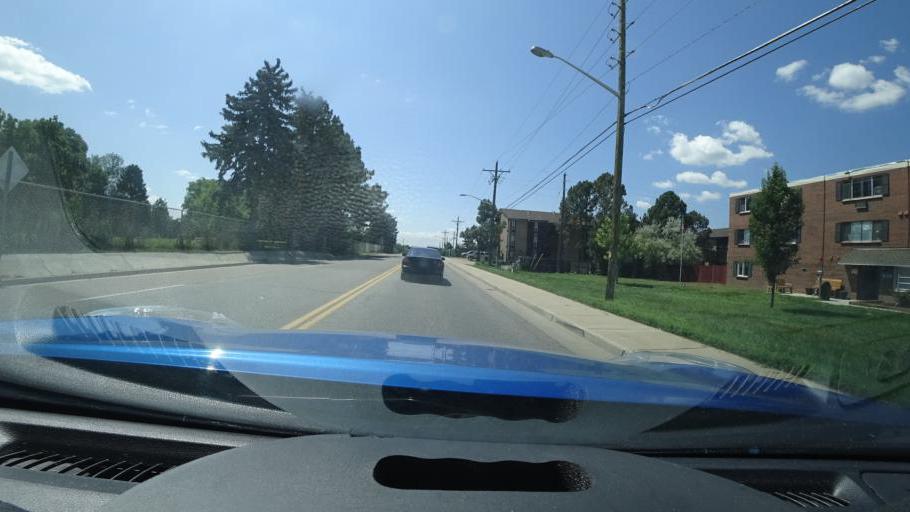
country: US
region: Colorado
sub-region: Arapahoe County
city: Glendale
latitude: 39.7016
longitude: -104.9035
